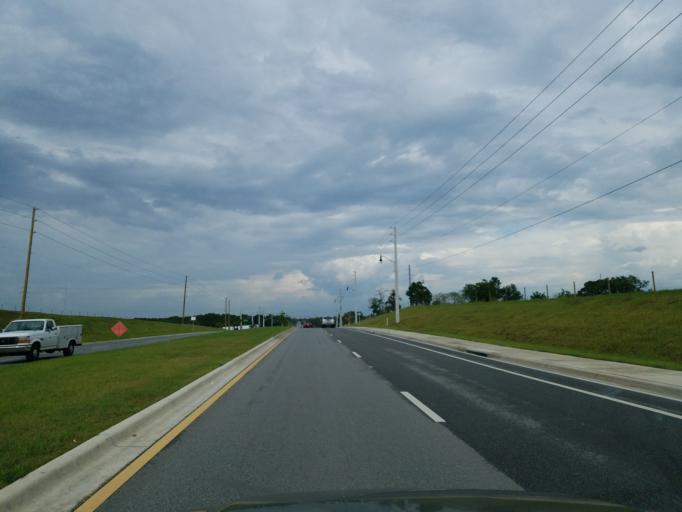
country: US
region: Florida
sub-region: Marion County
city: Ocala
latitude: 29.2233
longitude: -82.1711
